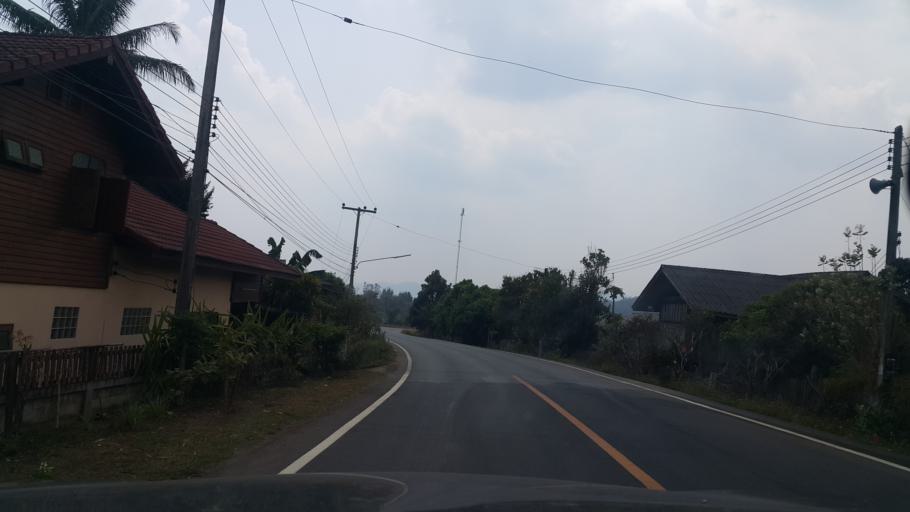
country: TH
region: Lamphun
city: Thung Hua Chang
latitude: 18.1345
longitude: 99.0136
